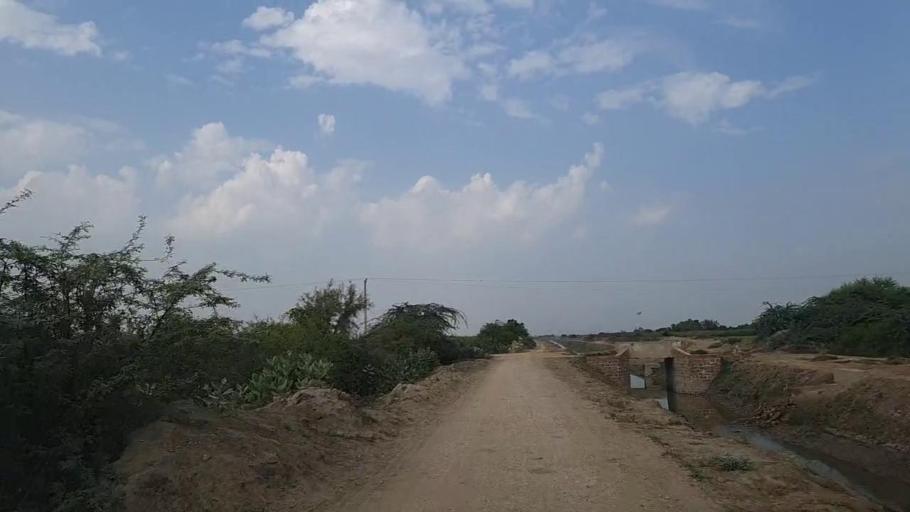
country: PK
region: Sindh
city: Daro Mehar
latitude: 24.7200
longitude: 68.1385
